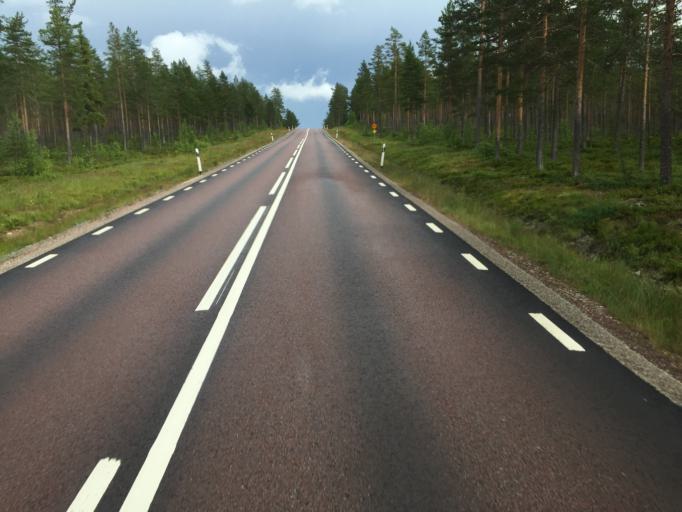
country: SE
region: Dalarna
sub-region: Malung-Saelens kommun
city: Malung
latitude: 60.8243
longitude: 14.0137
